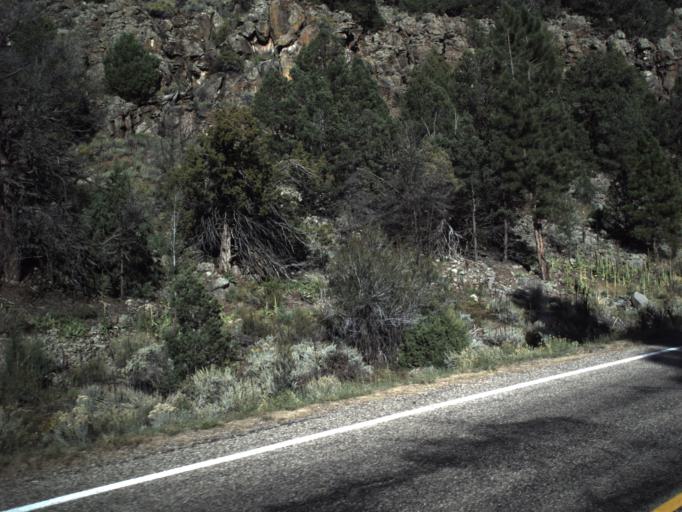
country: US
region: Utah
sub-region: Garfield County
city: Panguitch
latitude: 37.7677
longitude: -112.4634
